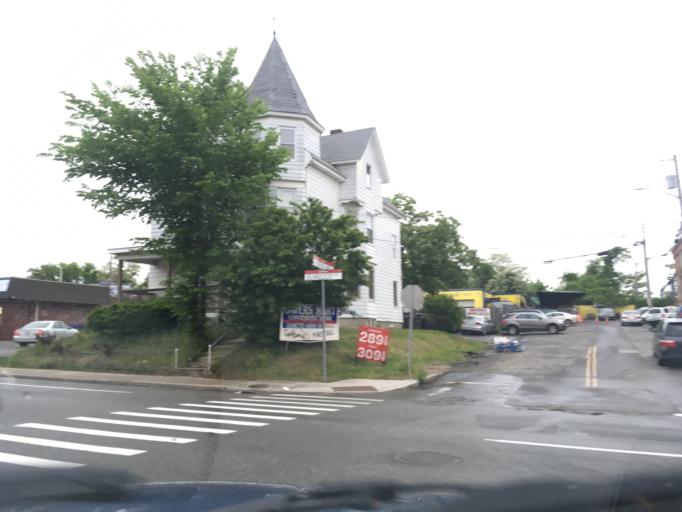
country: US
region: Rhode Island
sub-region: Providence County
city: Cranston
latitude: 41.7892
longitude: -71.4213
